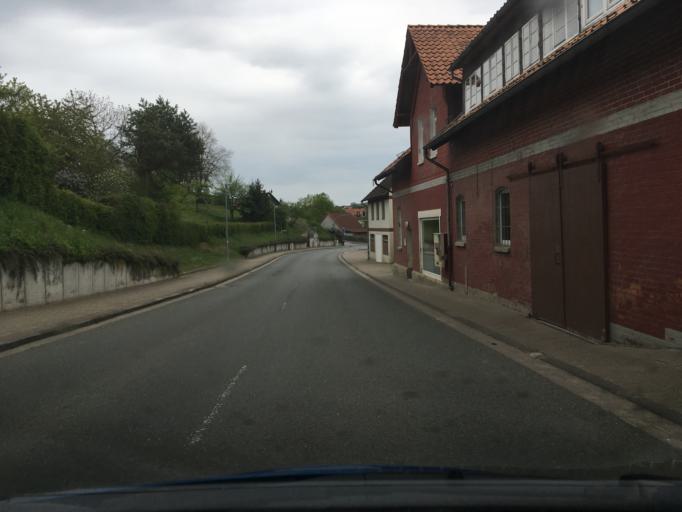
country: DE
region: Lower Saxony
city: Delligsen
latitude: 51.9449
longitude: 9.7978
